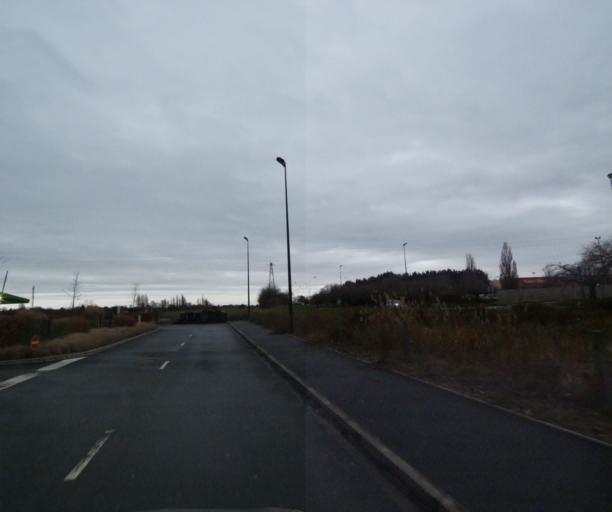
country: FR
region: Nord-Pas-de-Calais
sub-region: Departement du Nord
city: Raismes
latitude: 50.3798
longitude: 3.4794
